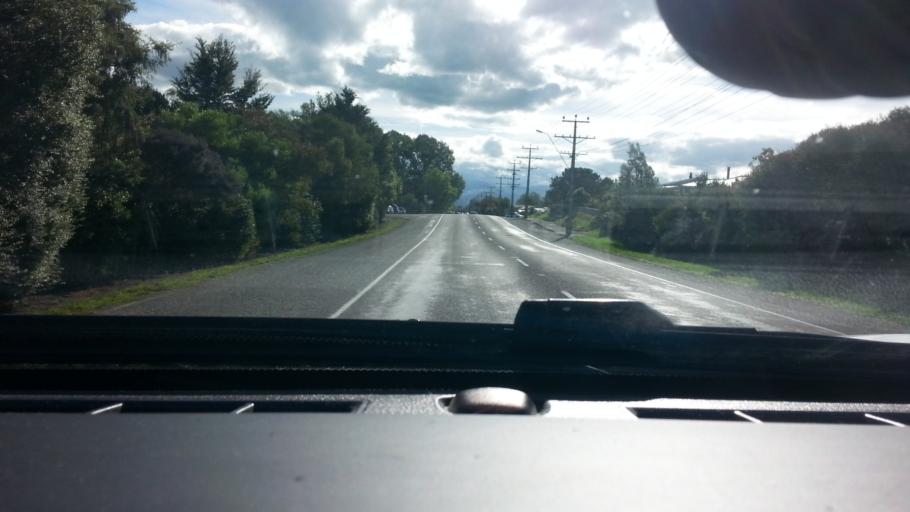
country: NZ
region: Wellington
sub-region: Masterton District
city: Masterton
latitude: -40.9489
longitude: 175.6835
